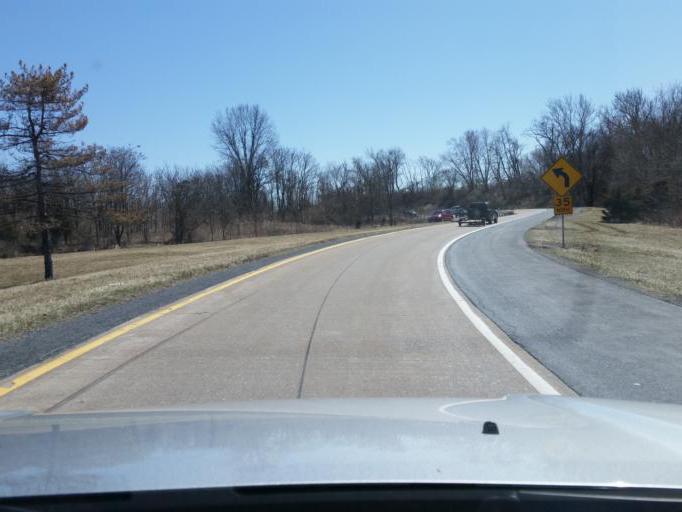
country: US
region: Pennsylvania
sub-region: Dauphin County
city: Middletown
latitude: 40.2245
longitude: -76.7228
